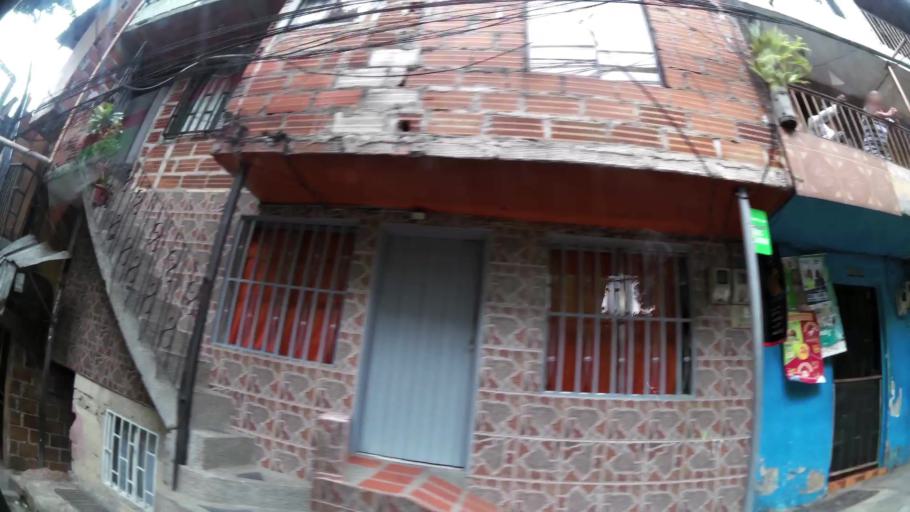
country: CO
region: Antioquia
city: Medellin
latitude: 6.2698
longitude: -75.5992
